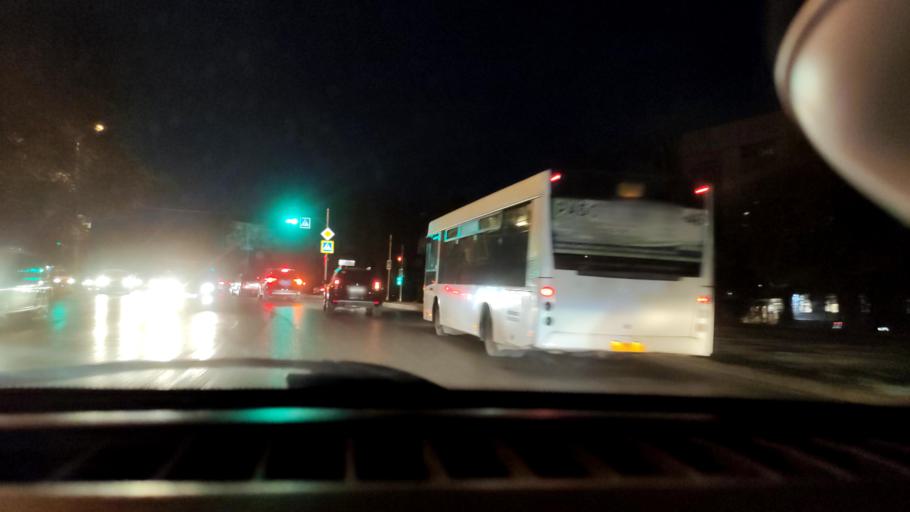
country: RU
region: Samara
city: Samara
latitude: 53.2139
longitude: 50.2121
